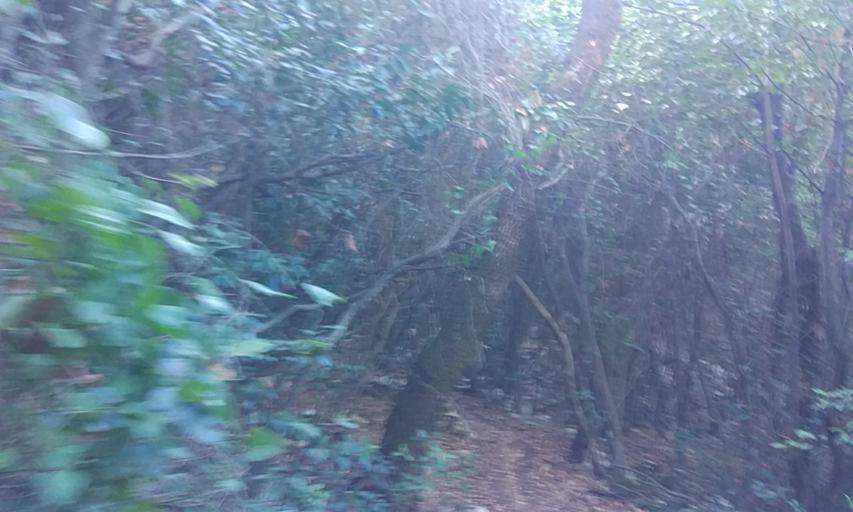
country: TR
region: Antalya
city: Tekirova
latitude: 36.3790
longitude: 30.4775
